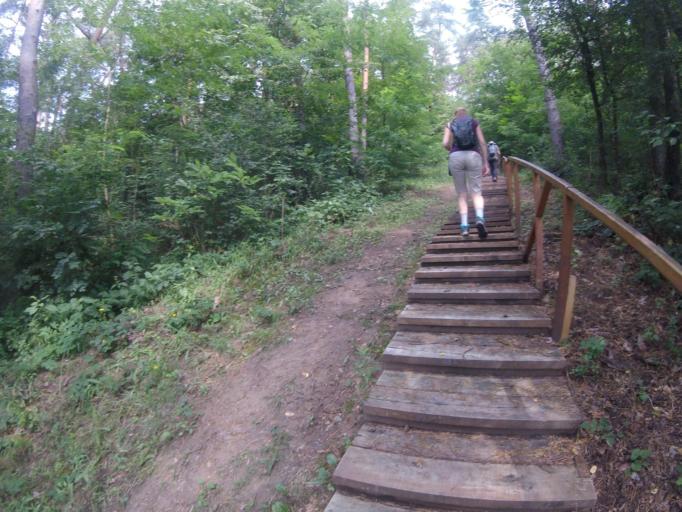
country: HU
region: Borsod-Abauj-Zemplen
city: Sarospatak
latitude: 48.4485
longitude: 21.5249
